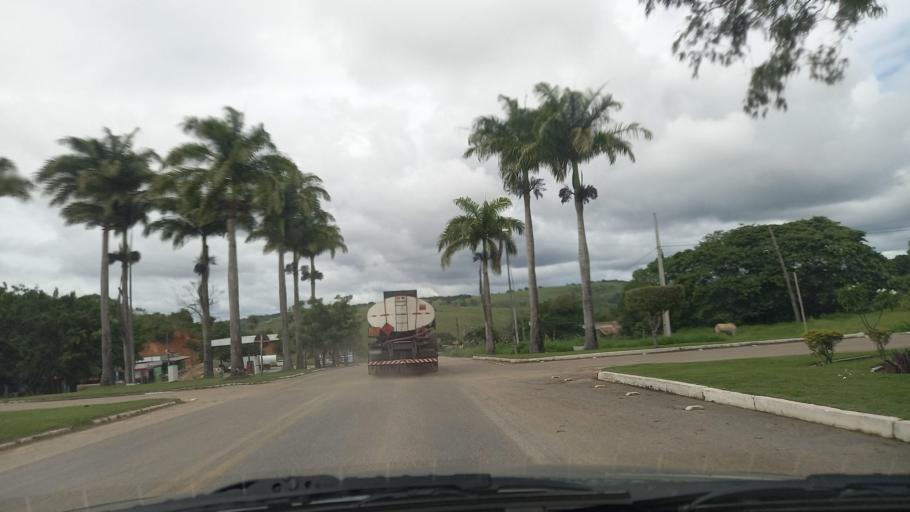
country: BR
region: Pernambuco
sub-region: Canhotinho
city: Canhotinho
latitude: -8.8729
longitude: -36.2005
